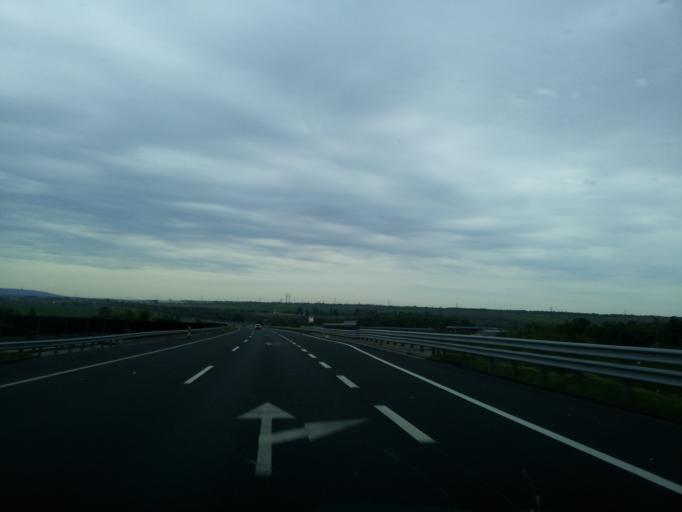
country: HU
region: Pest
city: Szazhalombatta
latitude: 47.3338
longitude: 18.8893
